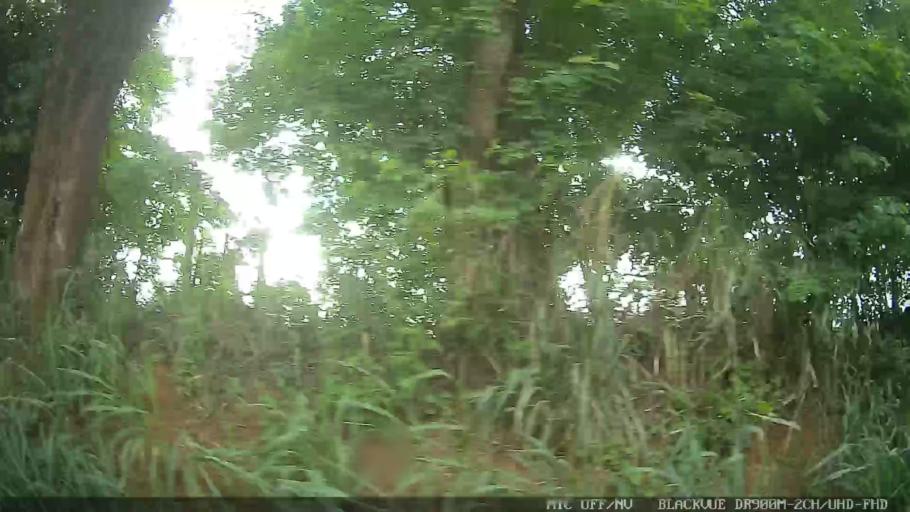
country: BR
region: Sao Paulo
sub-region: Atibaia
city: Atibaia
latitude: -23.1100
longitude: -46.6152
